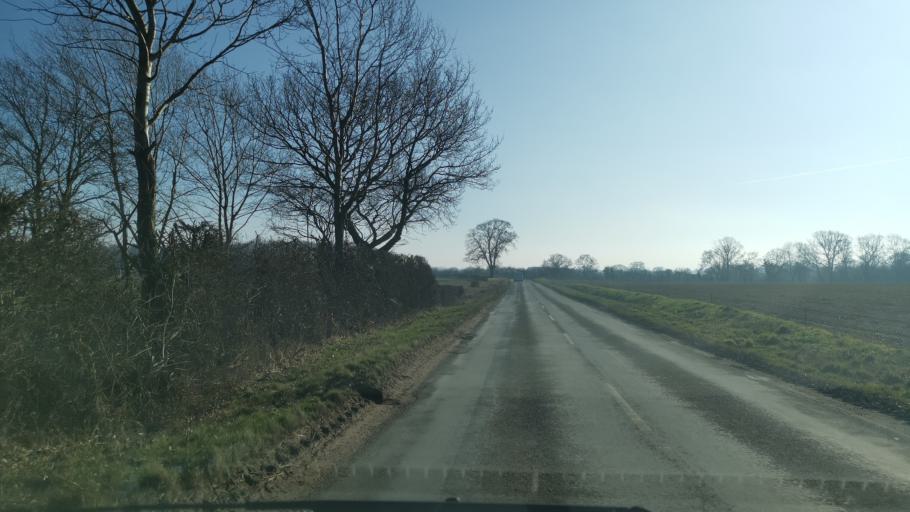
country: GB
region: England
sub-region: City of York
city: Murton
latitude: 53.9836
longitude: -1.0108
